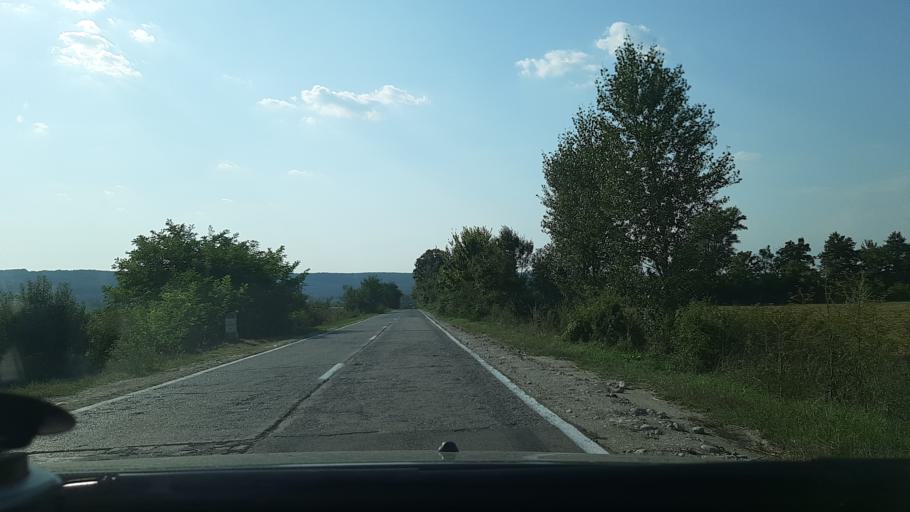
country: RO
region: Gorj
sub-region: Comuna Targu Carbunesti
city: Targu Carbunesti
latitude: 44.9440
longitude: 23.5262
